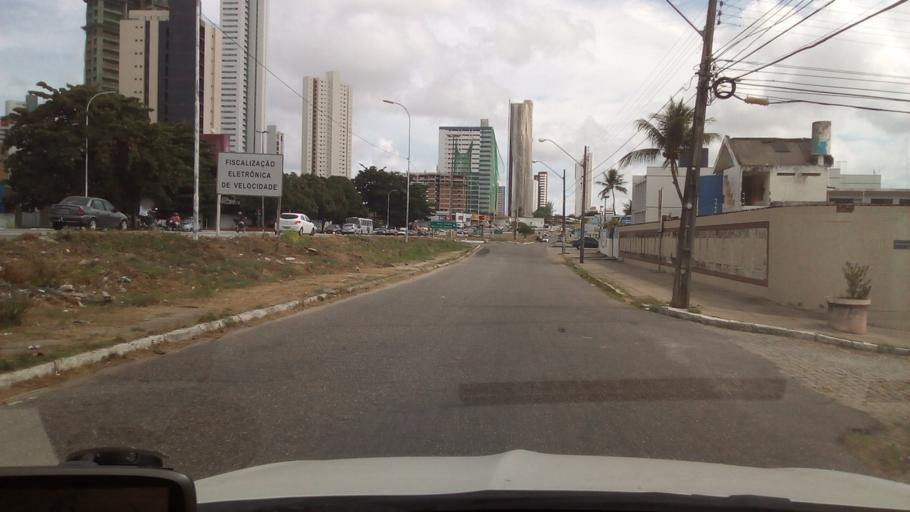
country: BR
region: Paraiba
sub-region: Joao Pessoa
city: Joao Pessoa
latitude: -7.1122
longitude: -34.8428
